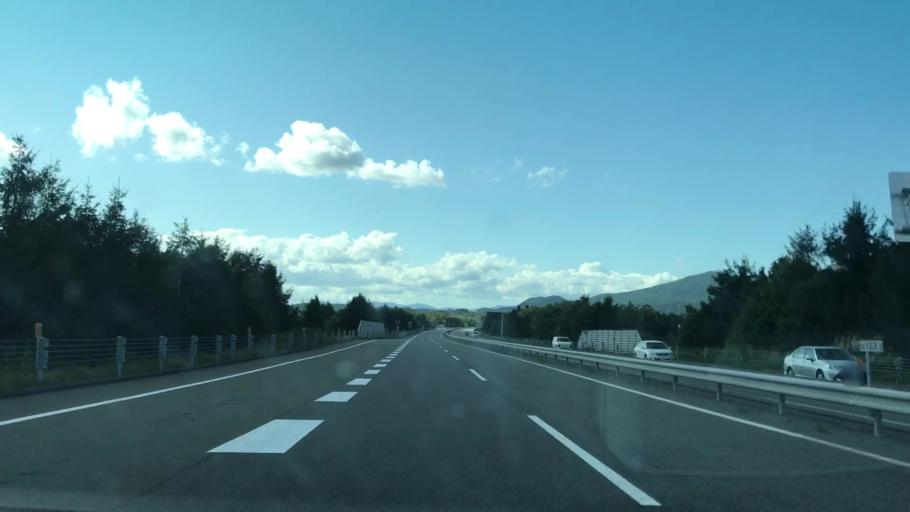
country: JP
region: Hokkaido
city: Date
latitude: 42.4861
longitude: 140.8895
